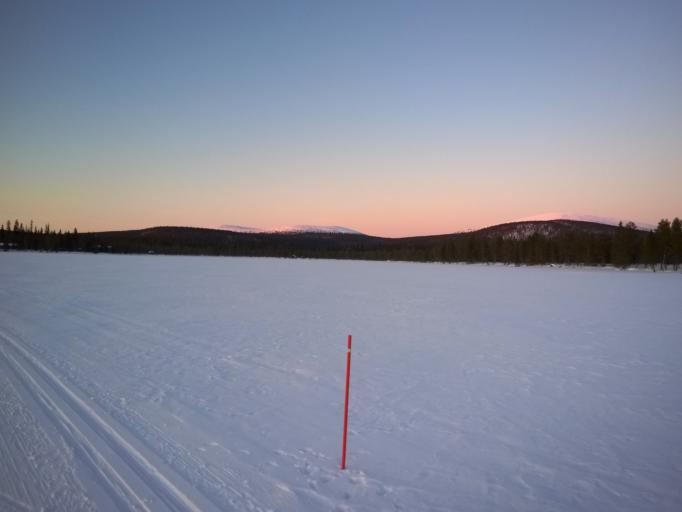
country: FI
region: Lapland
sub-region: Tunturi-Lappi
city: Muonio
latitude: 67.9302
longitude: 24.0469
